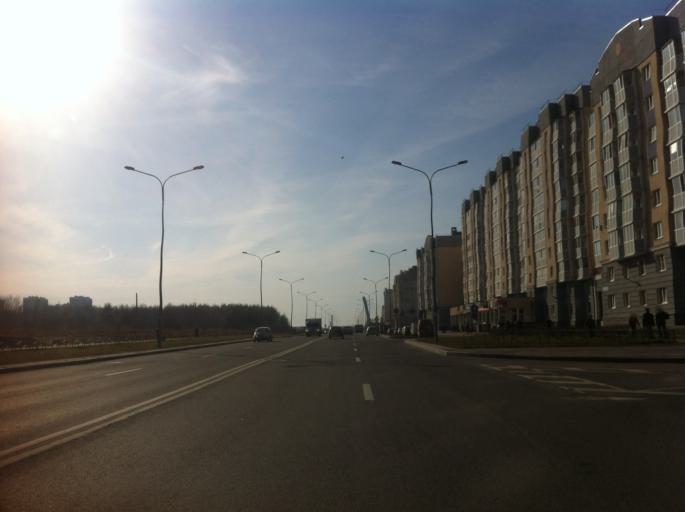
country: RU
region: St.-Petersburg
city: Uritsk
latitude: 59.8576
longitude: 30.1743
